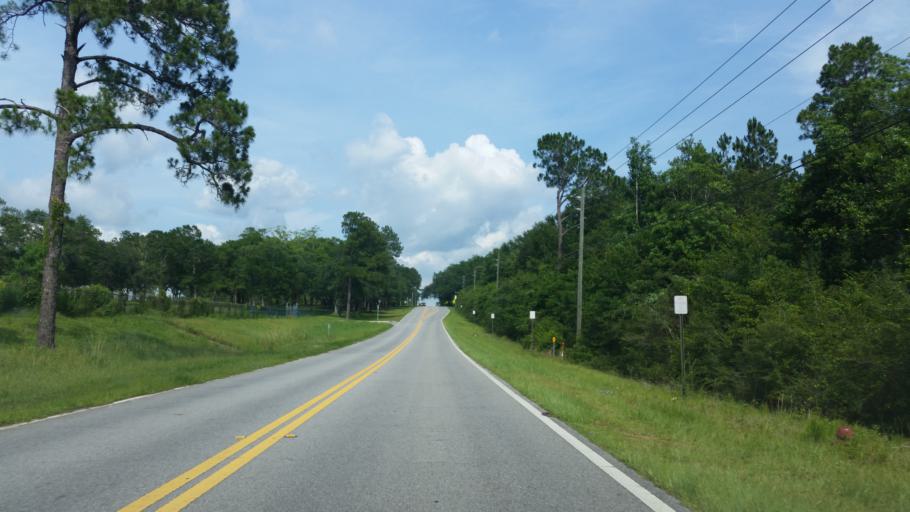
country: US
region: Florida
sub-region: Escambia County
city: Cantonment
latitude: 30.5784
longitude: -87.3442
